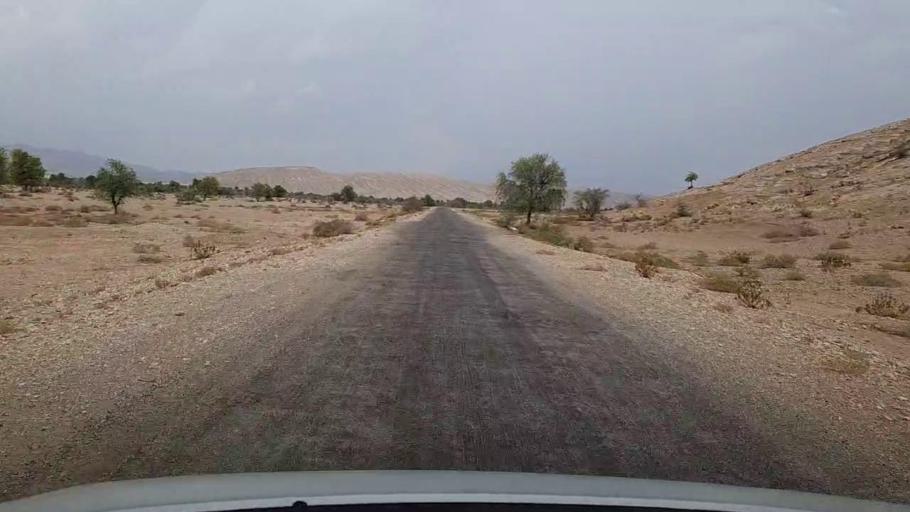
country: PK
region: Sindh
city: Sehwan
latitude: 26.2250
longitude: 67.7109
